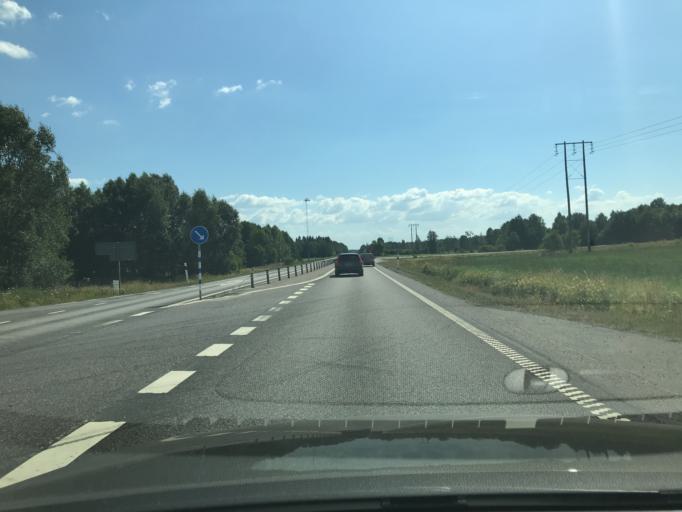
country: SE
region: Kronoberg
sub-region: Almhults Kommun
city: AElmhult
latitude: 56.5001
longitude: 14.1223
